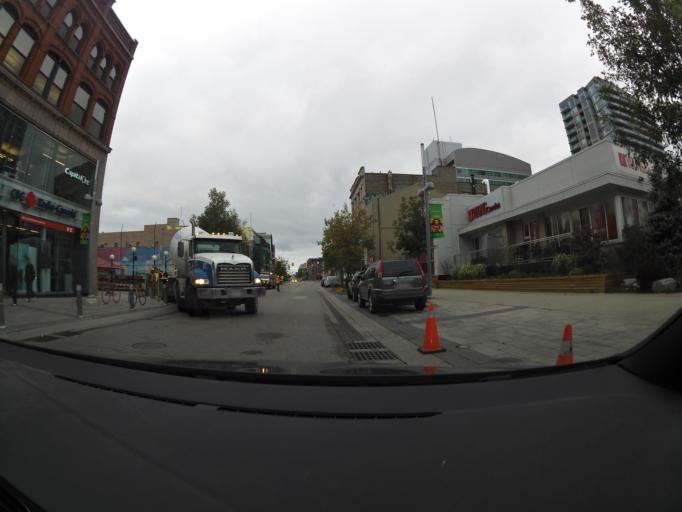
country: CA
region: Ontario
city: Waterloo
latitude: 43.4506
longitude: -80.4911
